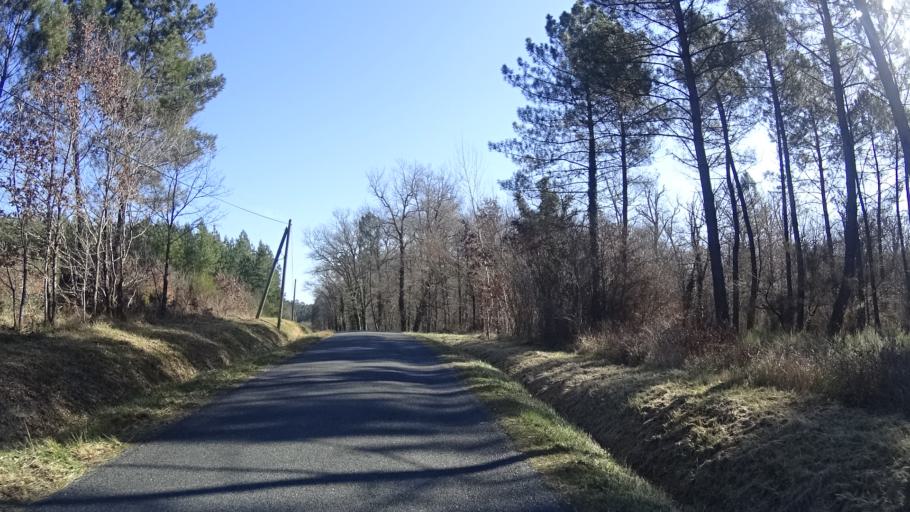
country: FR
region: Aquitaine
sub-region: Departement de la Dordogne
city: Saint-Aulaye
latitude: 45.1219
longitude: 0.2113
